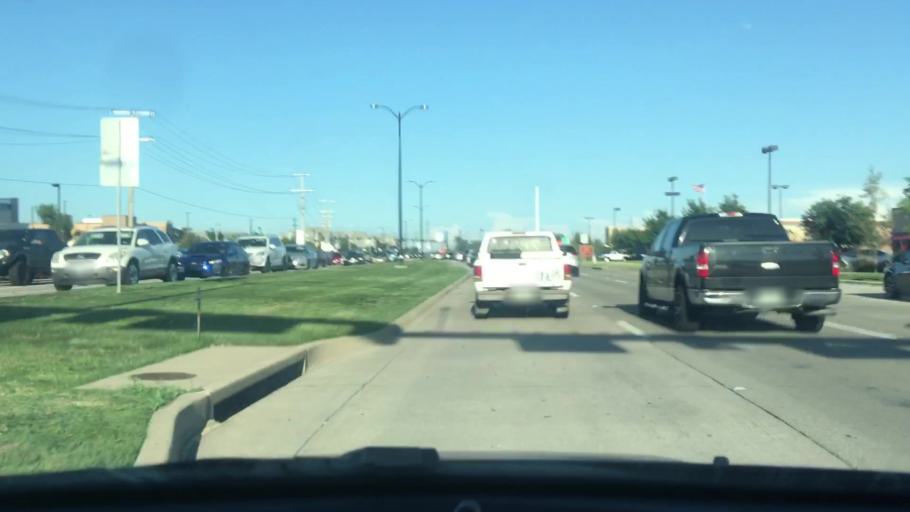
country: US
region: Texas
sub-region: Collin County
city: Frisco
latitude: 33.1749
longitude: -96.8389
